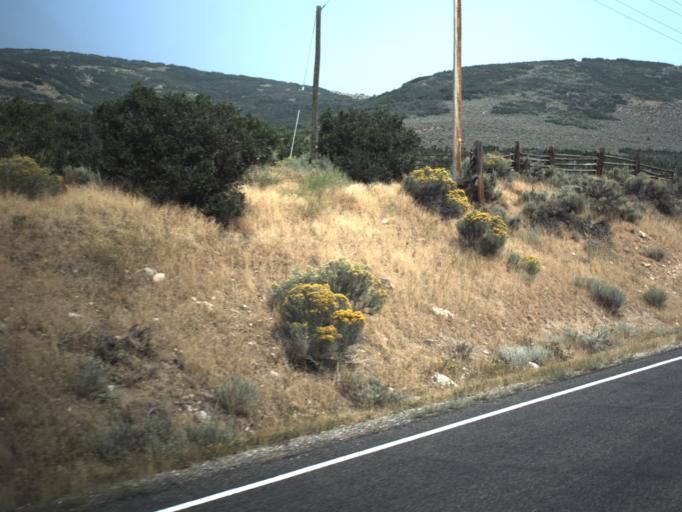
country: US
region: Utah
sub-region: Summit County
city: Kamas
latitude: 40.6398
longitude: -111.2619
